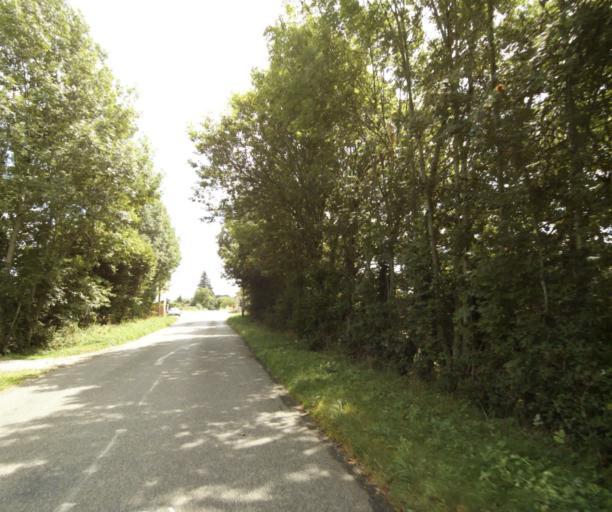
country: FR
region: Limousin
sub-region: Departement de la Correze
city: Sainte-Fortunade
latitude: 45.1902
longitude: 1.8128
